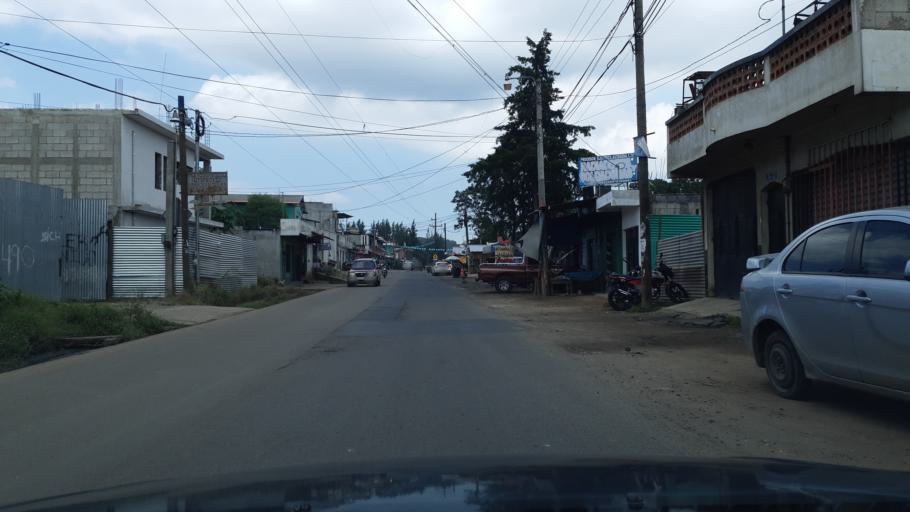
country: GT
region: Chimaltenango
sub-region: Municipio de Chimaltenango
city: Chimaltenango
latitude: 14.6768
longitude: -90.8010
